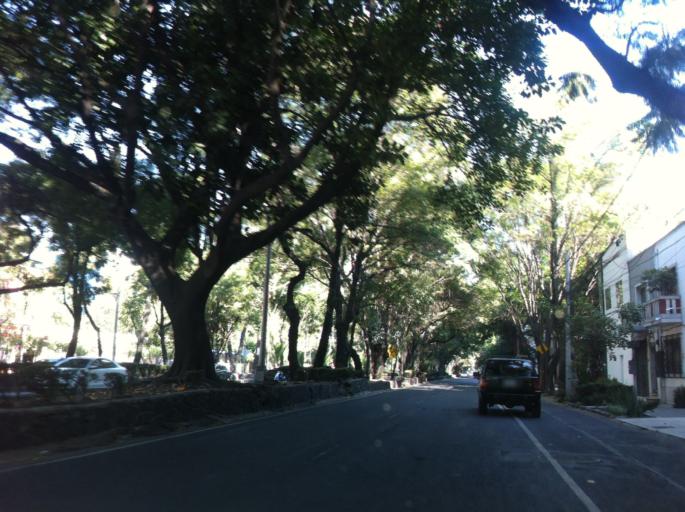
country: MX
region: Mexico City
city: Miguel Hidalgo
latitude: 19.4380
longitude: -99.1954
